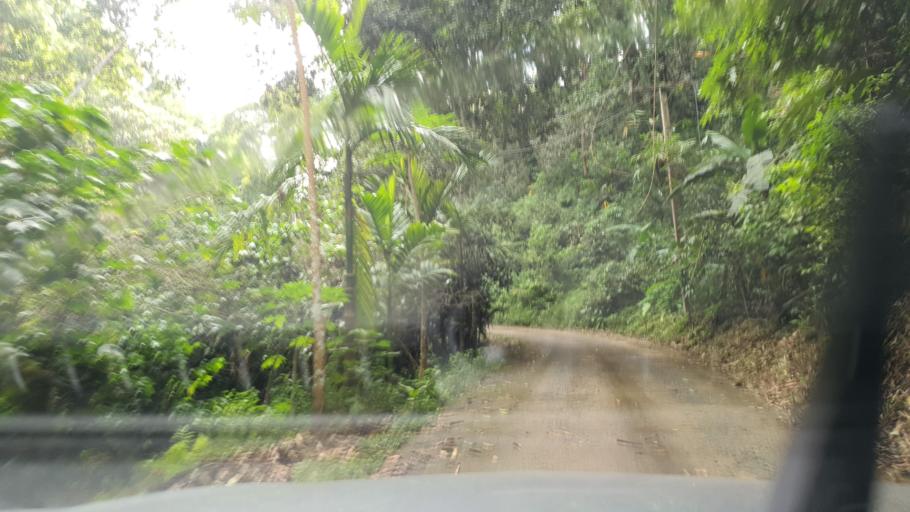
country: TH
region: Chiang Mai
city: Mae On
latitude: 18.9508
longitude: 99.3082
